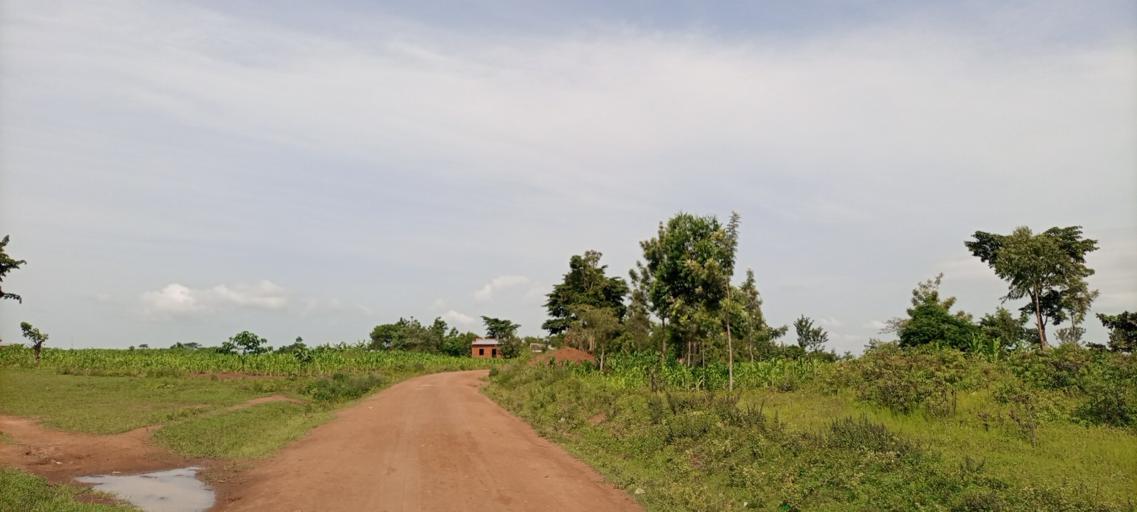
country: UG
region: Eastern Region
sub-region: Mbale District
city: Mbale
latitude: 1.1300
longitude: 34.0445
